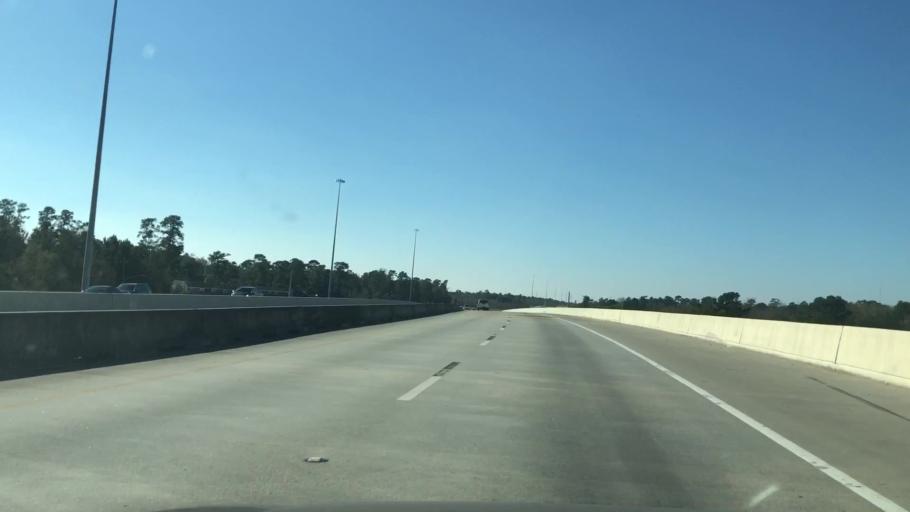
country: US
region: Texas
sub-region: Harris County
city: Cloverleaf
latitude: 29.8171
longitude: -95.2074
